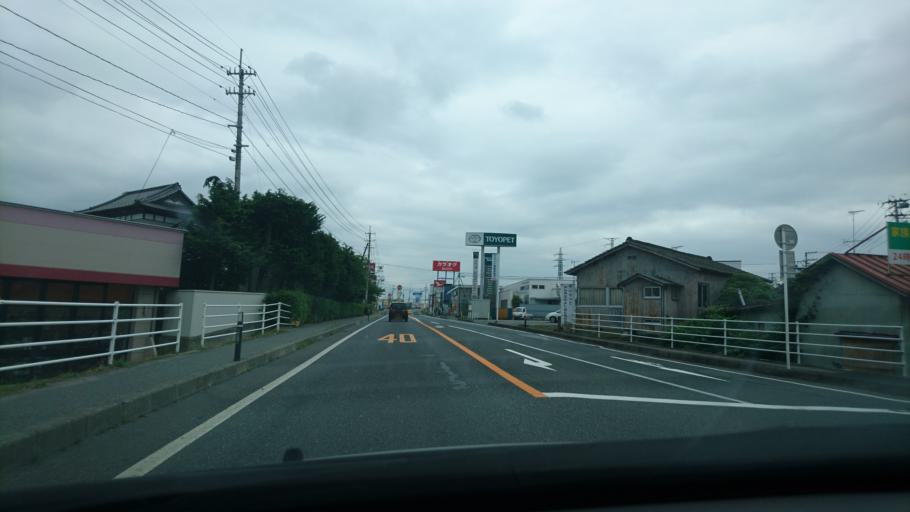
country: JP
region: Miyagi
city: Furukawa
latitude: 38.7400
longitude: 141.0194
